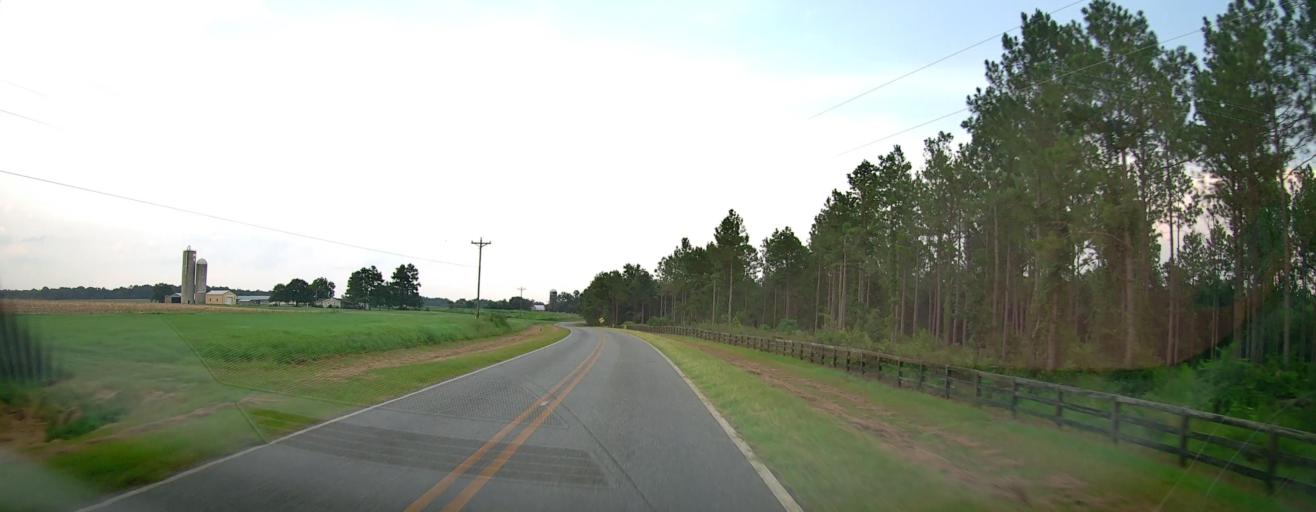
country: US
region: Georgia
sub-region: Laurens County
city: East Dublin
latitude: 32.6358
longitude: -82.8469
